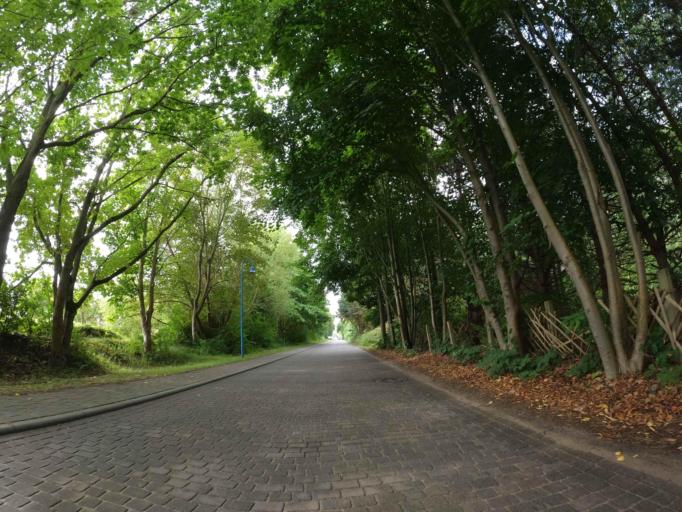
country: DE
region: Mecklenburg-Vorpommern
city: Ostseebad Gohren
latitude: 54.3213
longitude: 13.7258
